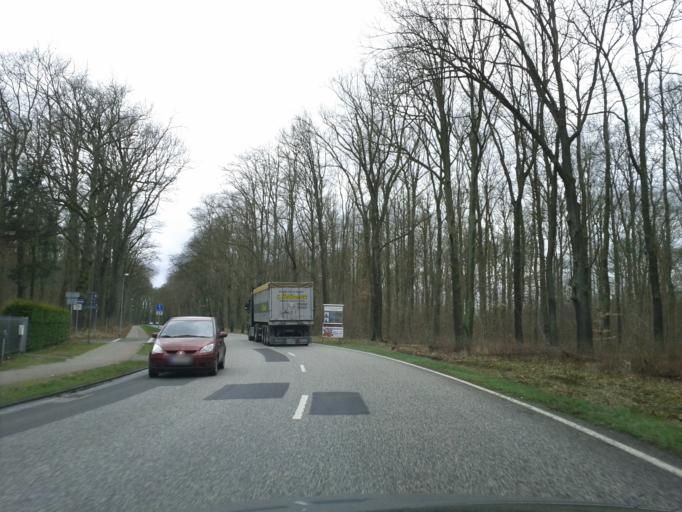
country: DE
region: Brandenburg
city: Spreenhagen
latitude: 52.3970
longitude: 13.9289
